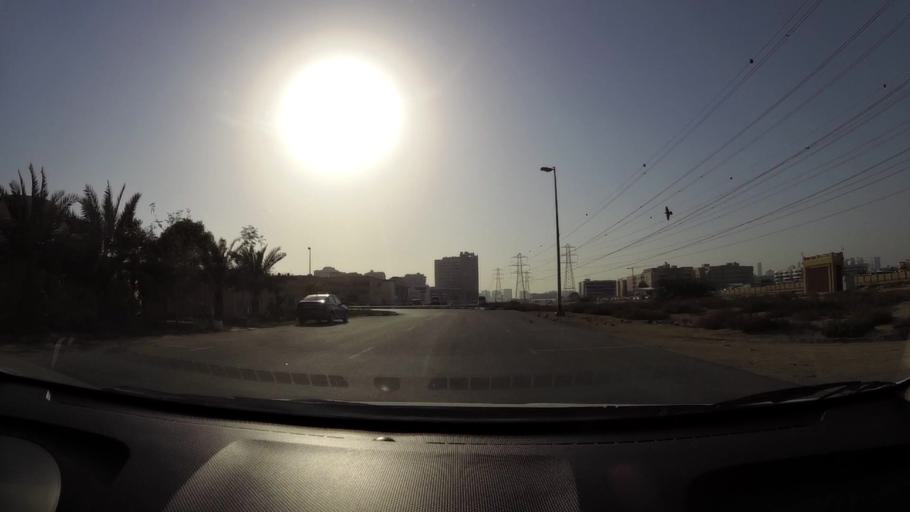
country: AE
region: Ash Shariqah
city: Sharjah
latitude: 25.2734
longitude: 55.3871
